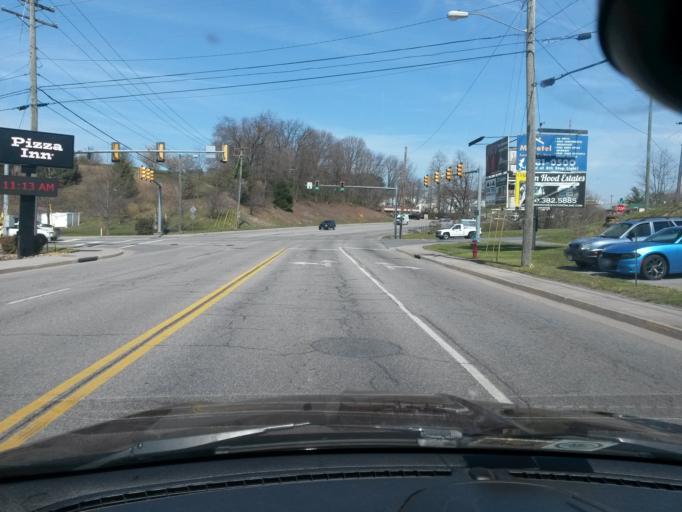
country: US
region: Virginia
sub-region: Montgomery County
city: Christiansburg
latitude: 37.1322
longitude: -80.4121
